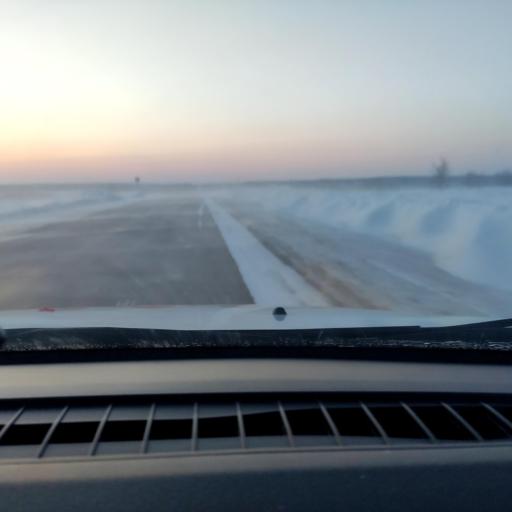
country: RU
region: Samara
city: Georgiyevka
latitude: 53.4176
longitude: 50.8648
